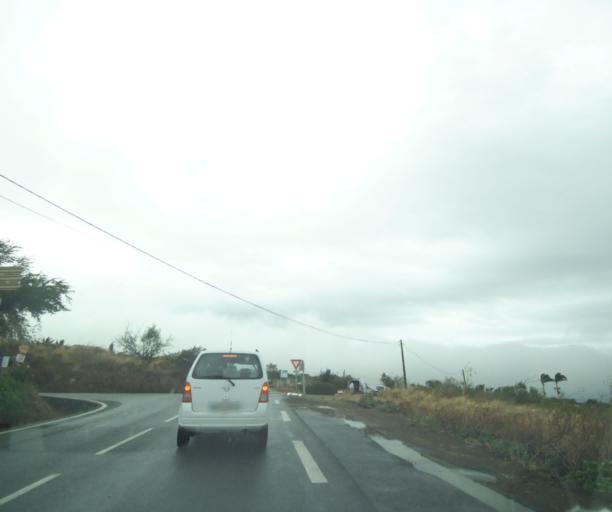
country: RE
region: Reunion
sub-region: Reunion
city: Saint-Paul
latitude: -21.0339
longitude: 55.2771
